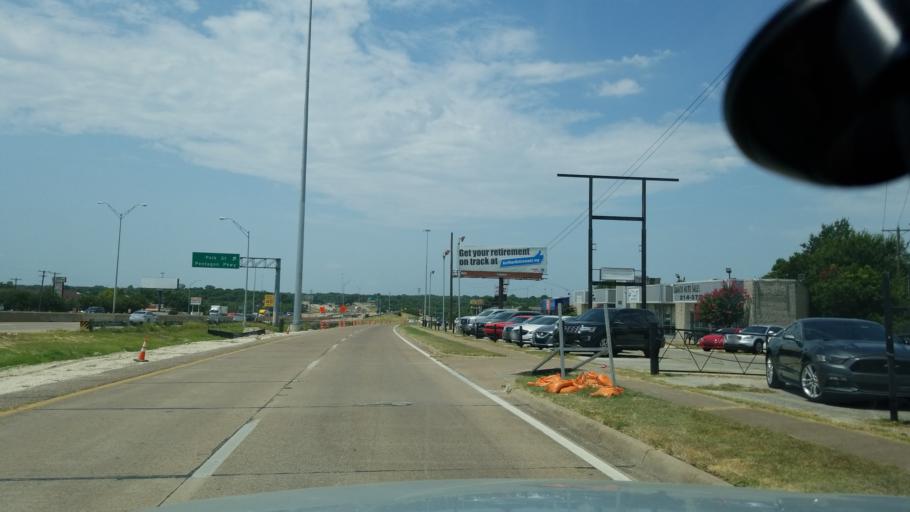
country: US
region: Texas
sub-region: Dallas County
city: Cockrell Hill
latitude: 32.7012
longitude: -96.8364
